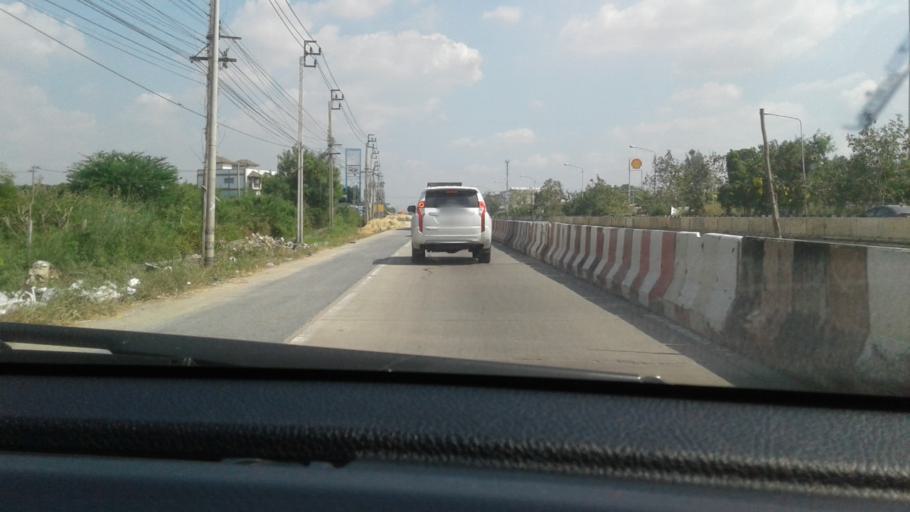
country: TH
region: Nonthaburi
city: Bang Bua Thong
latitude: 13.9419
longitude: 100.4220
